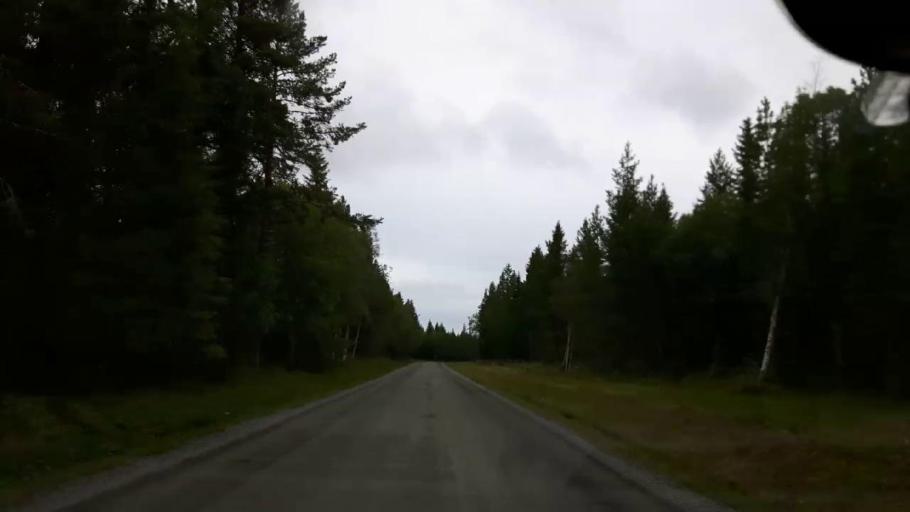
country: SE
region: Jaemtland
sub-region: OEstersunds Kommun
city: Ostersund
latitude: 63.1190
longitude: 14.5414
